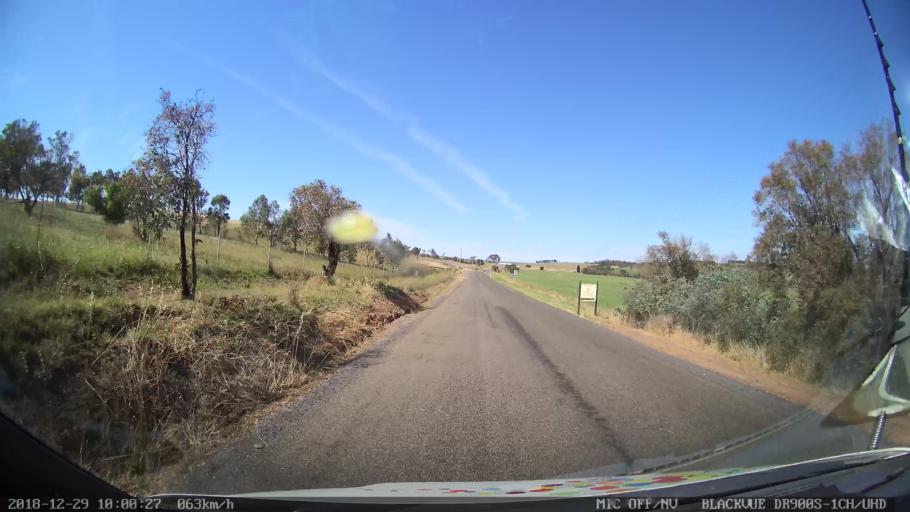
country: AU
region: New South Wales
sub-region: Goulburn Mulwaree
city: Goulburn
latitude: -34.7923
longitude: 149.4854
